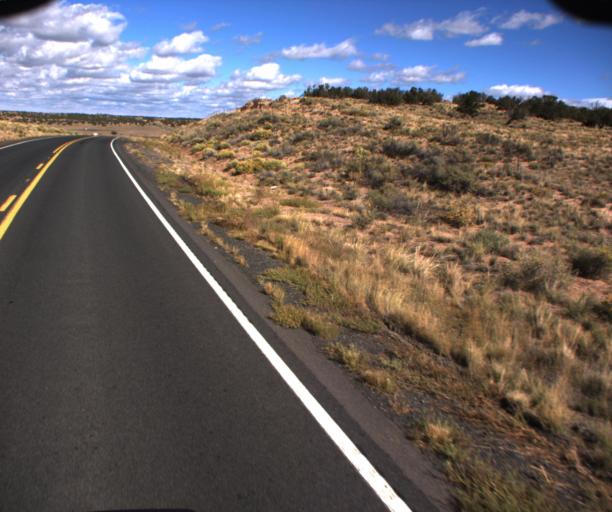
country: US
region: Arizona
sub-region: Apache County
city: Houck
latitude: 35.0876
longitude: -109.3105
